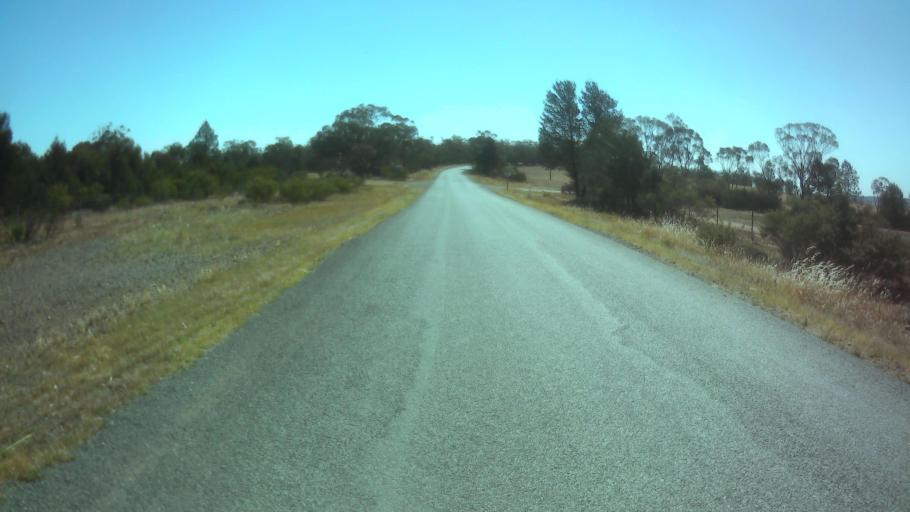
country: AU
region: New South Wales
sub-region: Weddin
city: Grenfell
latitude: -33.7553
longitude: 147.8302
